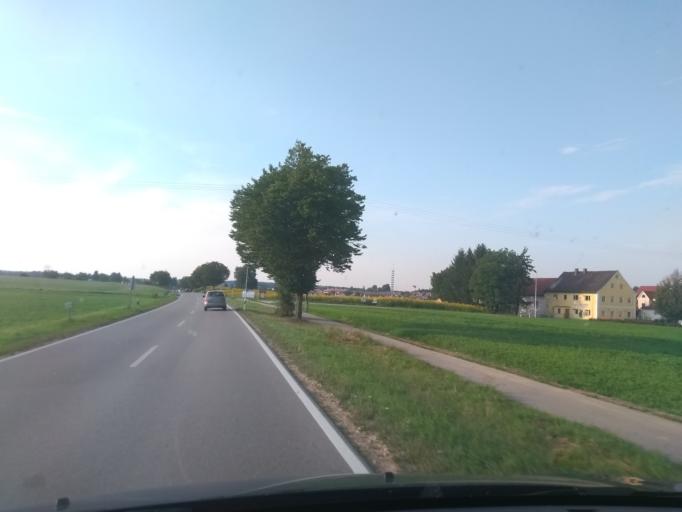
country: DE
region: Bavaria
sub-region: Upper Bavaria
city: Markt Indersdorf
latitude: 48.3429
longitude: 11.3874
